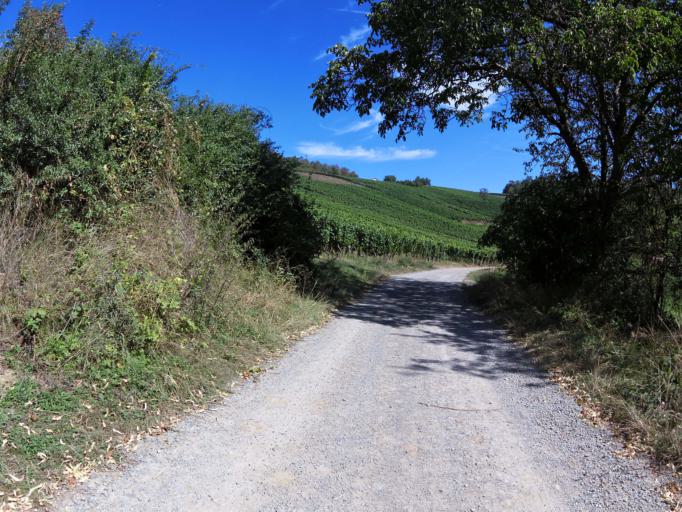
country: DE
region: Bavaria
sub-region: Regierungsbezirk Unterfranken
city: Thungersheim
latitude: 49.8733
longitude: 9.8700
